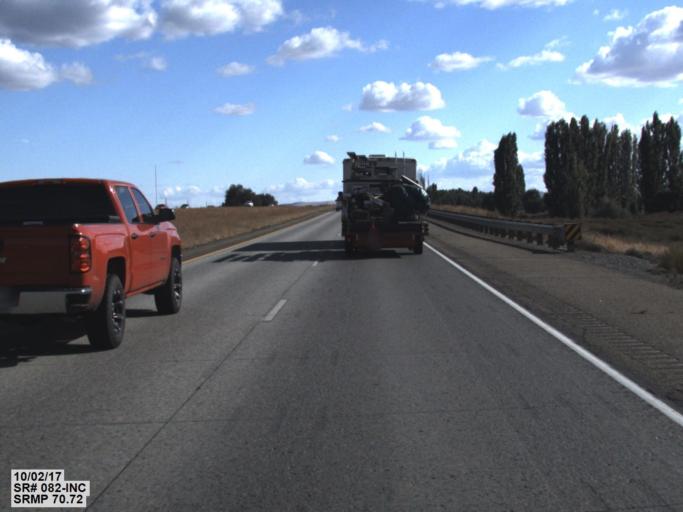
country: US
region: Washington
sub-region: Yakima County
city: Grandview
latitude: 46.2903
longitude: -119.9510
